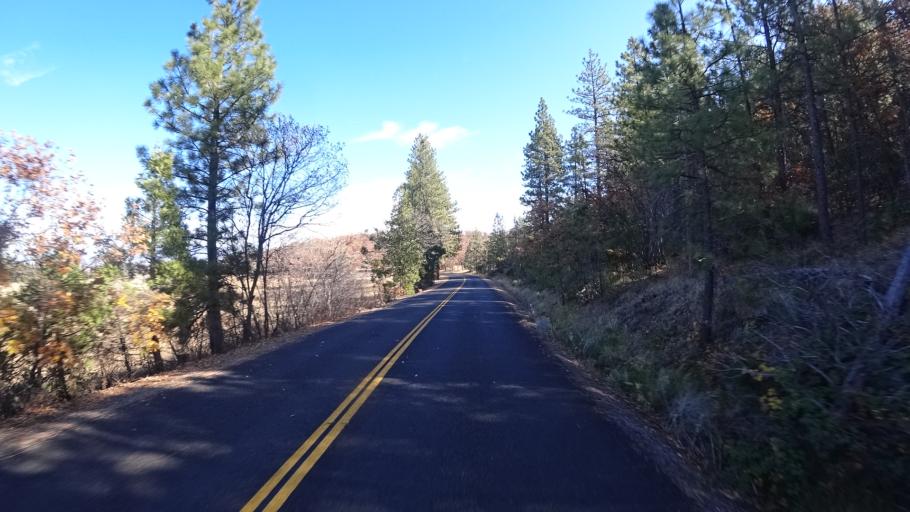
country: US
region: California
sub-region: Siskiyou County
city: Weed
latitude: 41.4364
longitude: -122.4584
